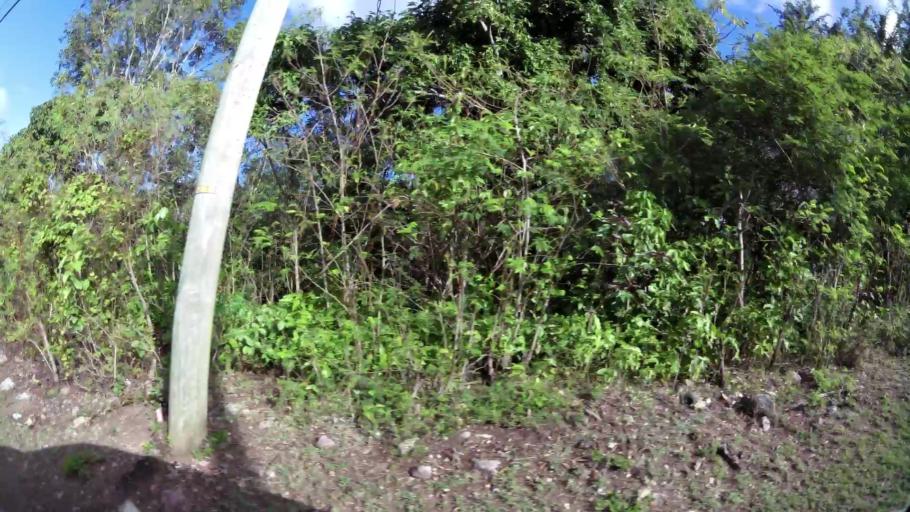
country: KN
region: Saint Paul Charlestown
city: Charlestown
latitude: 17.1280
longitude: -62.6059
